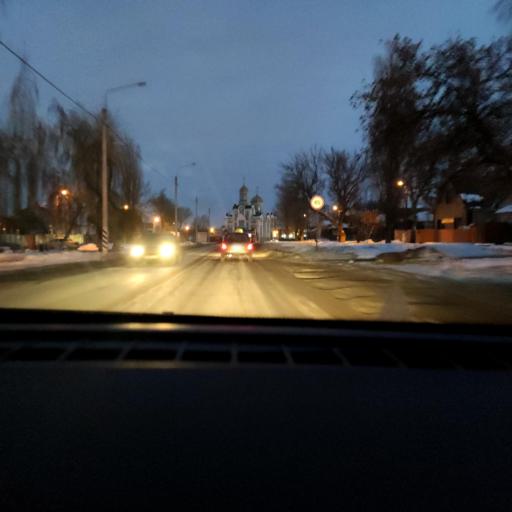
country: RU
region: Voronezj
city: Maslovka
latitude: 51.5538
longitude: 39.2366
